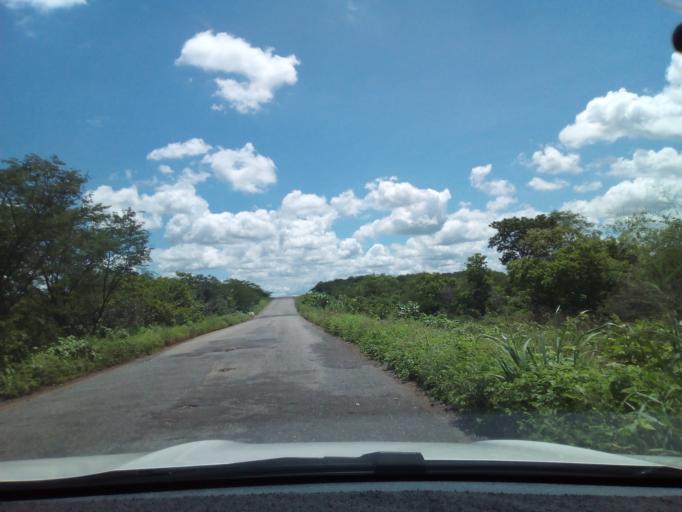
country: BR
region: Rio Grande do Norte
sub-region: Caico
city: Caico
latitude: -6.4325
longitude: -37.2143
